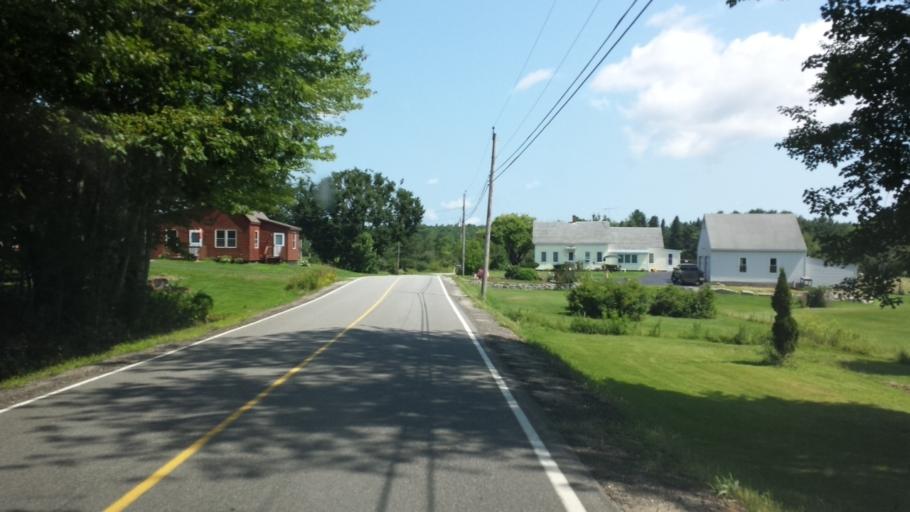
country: US
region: Maine
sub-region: York County
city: Biddeford
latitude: 43.4568
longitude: -70.5096
